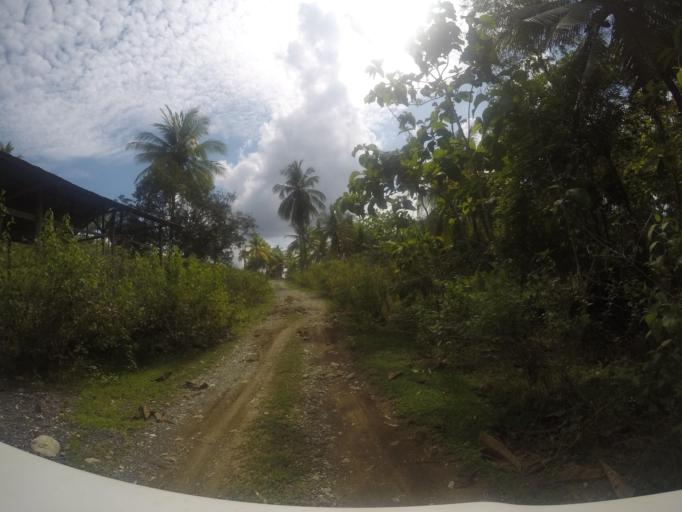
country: TL
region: Viqueque
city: Viqueque
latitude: -8.8501
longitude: 126.3602
